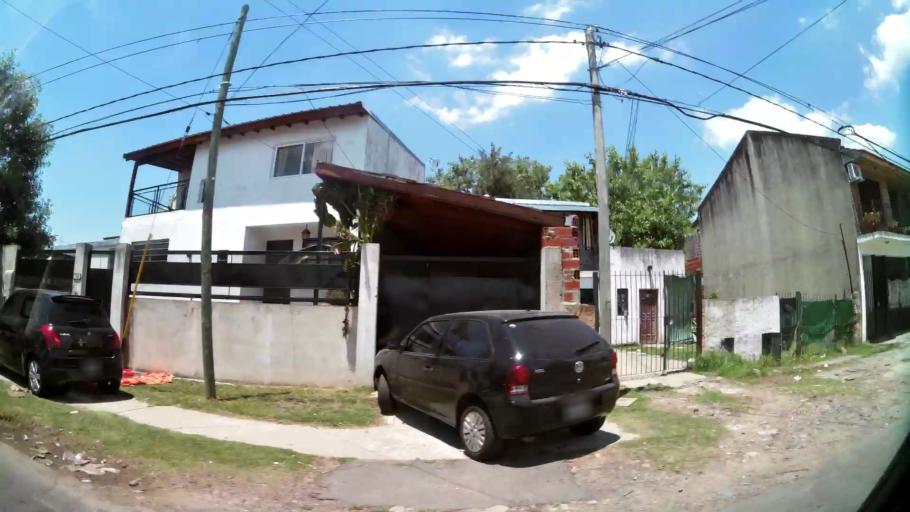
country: AR
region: Buenos Aires
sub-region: Partido de Tigre
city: Tigre
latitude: -34.4144
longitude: -58.5966
